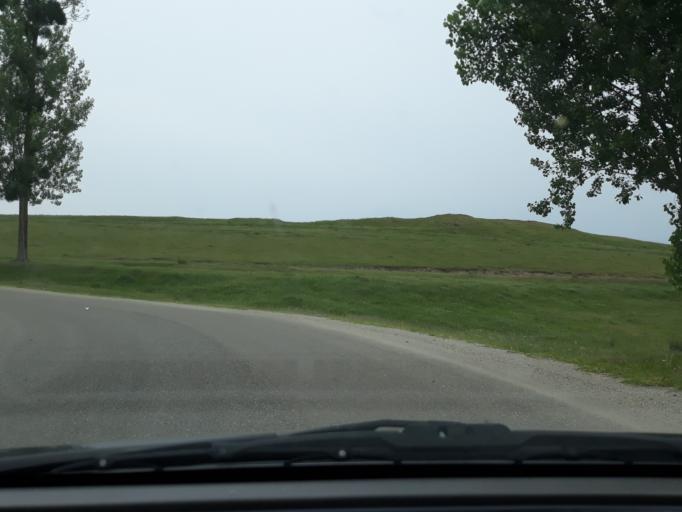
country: RO
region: Salaj
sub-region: Comuna Criseni
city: Criseni
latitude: 47.2438
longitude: 23.0682
